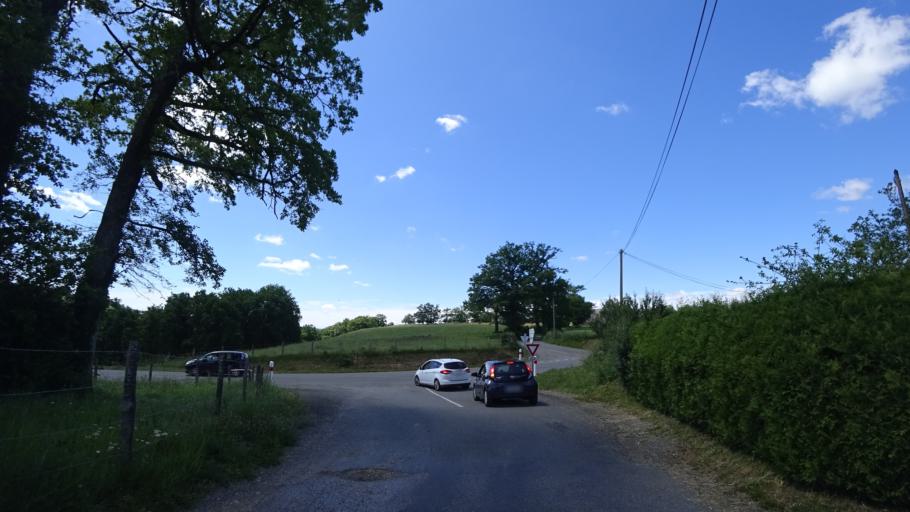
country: FR
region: Midi-Pyrenees
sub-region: Departement de l'Aveyron
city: Colombies
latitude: 44.3933
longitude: 2.3064
